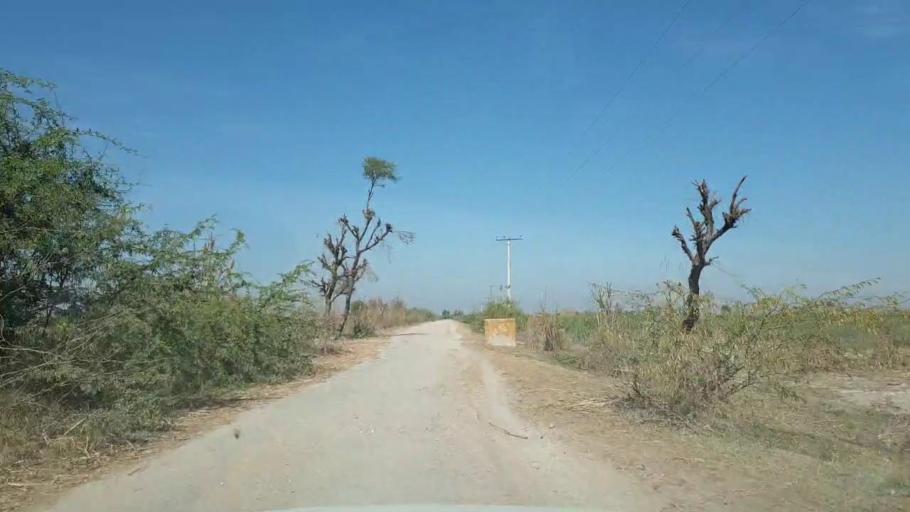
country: PK
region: Sindh
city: Pithoro
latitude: 25.6214
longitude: 69.2156
